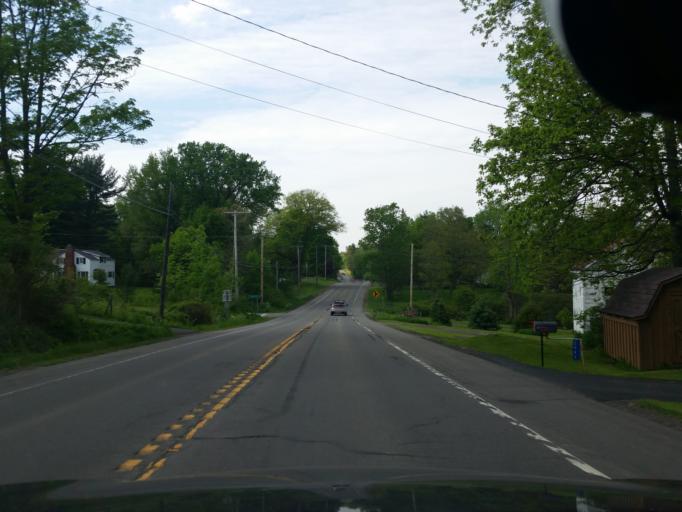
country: US
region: New York
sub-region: Chautauqua County
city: Lakewood
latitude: 42.1282
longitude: -79.3941
